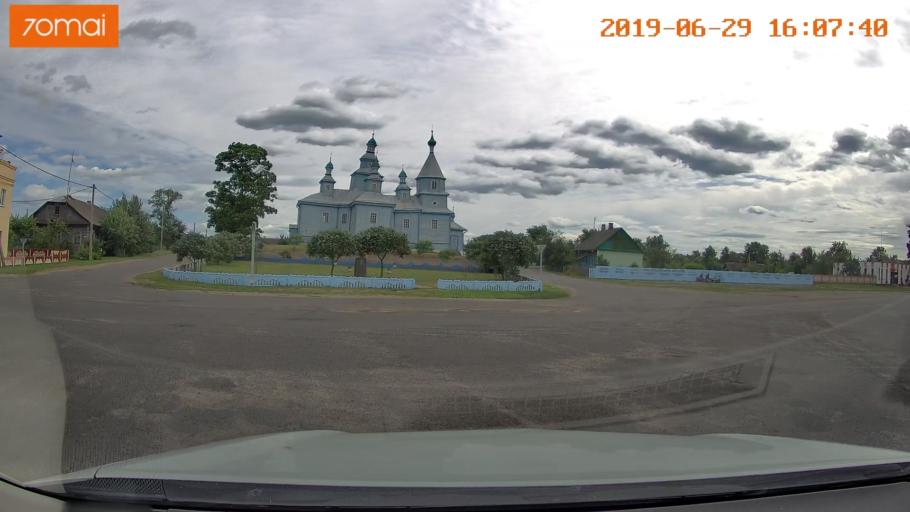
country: BY
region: Brest
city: Luninyets
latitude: 52.2060
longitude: 27.0101
